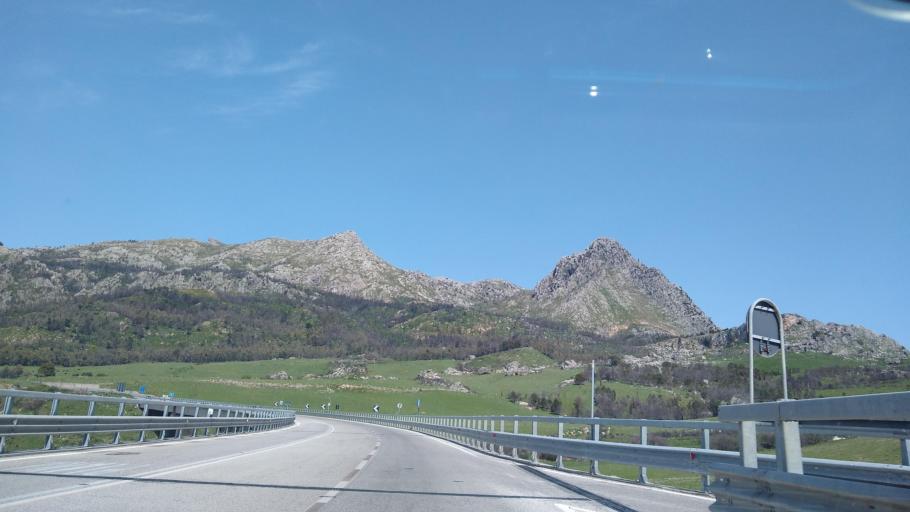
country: IT
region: Sicily
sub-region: Palermo
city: San Giuseppe Jato
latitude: 37.9822
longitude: 13.2354
